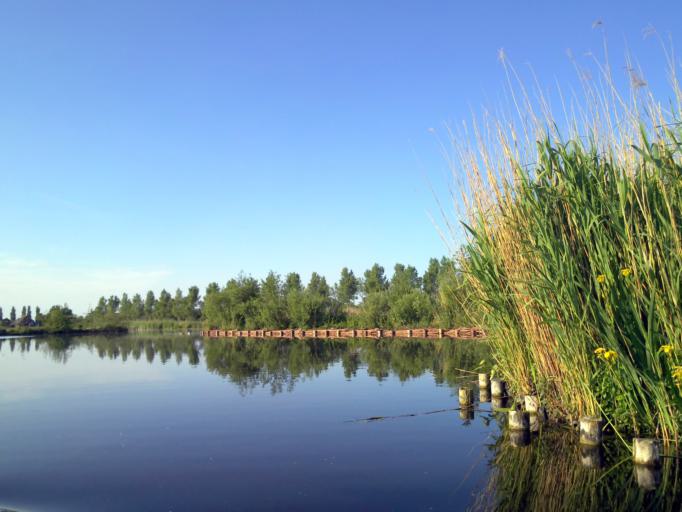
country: NL
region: Utrecht
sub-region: Gemeente De Ronde Venen
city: Mijdrecht
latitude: 52.1910
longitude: 4.9151
